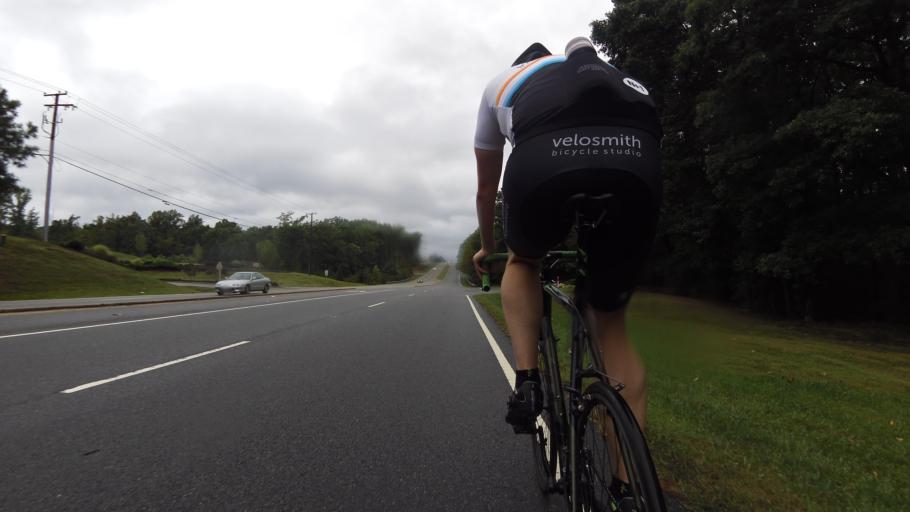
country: US
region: Virginia
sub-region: Henrico County
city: Short Pump
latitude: 37.5987
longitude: -77.6412
